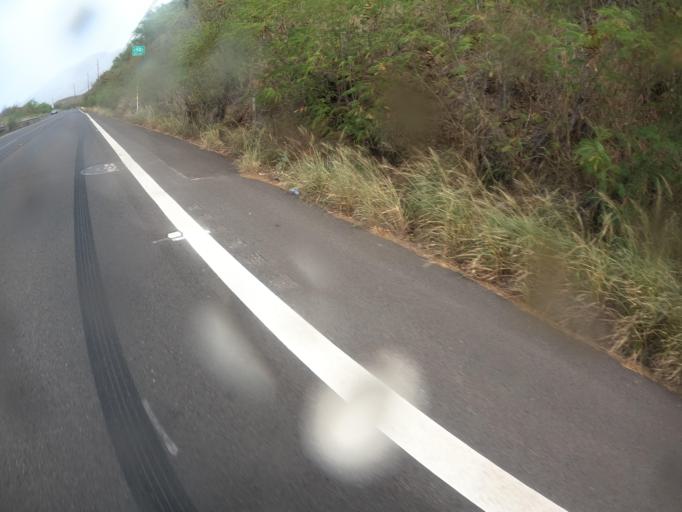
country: US
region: Hawaii
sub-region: Honolulu County
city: Makaha Valley
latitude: 21.5426
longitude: -158.2370
